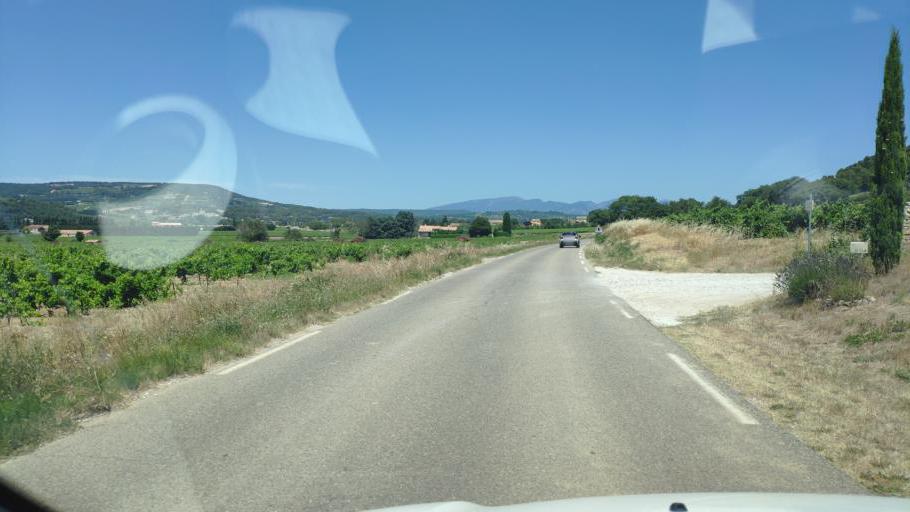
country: FR
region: Provence-Alpes-Cote d'Azur
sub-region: Departement du Vaucluse
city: Sablet
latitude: 44.2252
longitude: 5.0174
